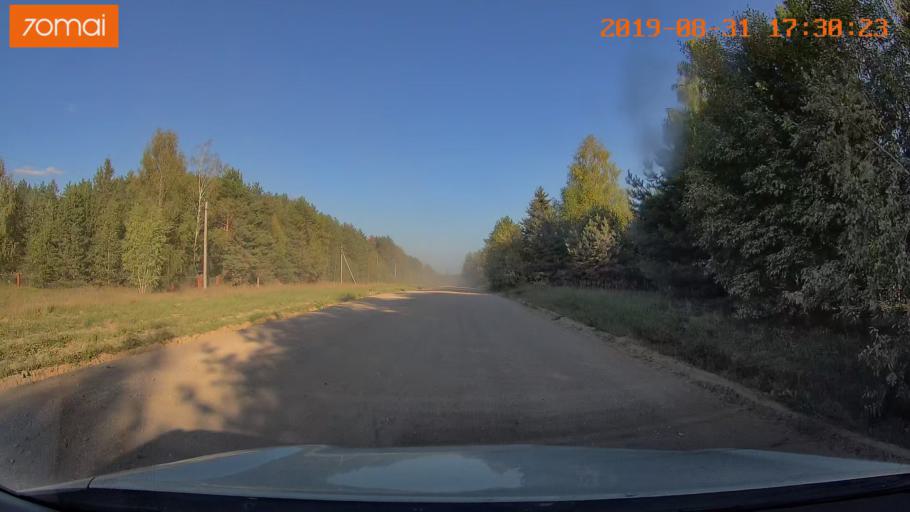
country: RU
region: Kaluga
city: Detchino
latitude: 54.8109
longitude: 36.3343
